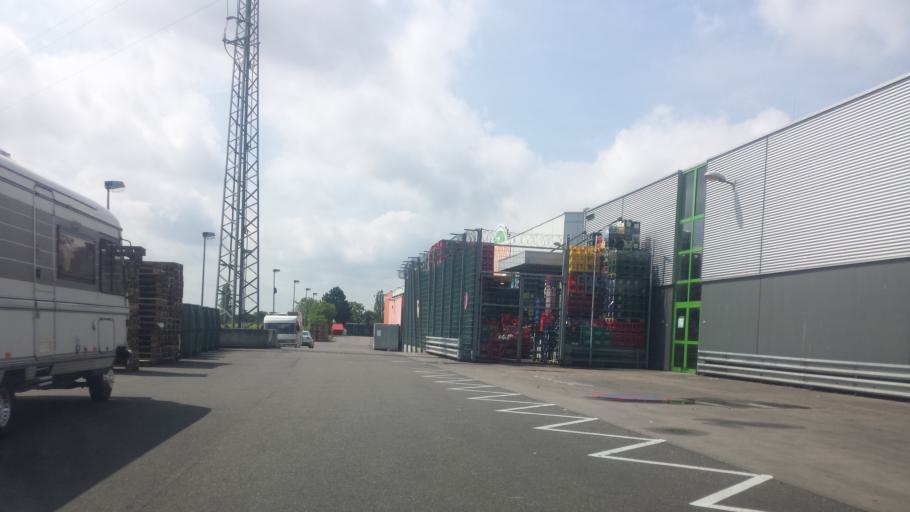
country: DE
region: Rheinland-Pfalz
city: Neustadt
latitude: 49.3401
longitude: 8.1627
